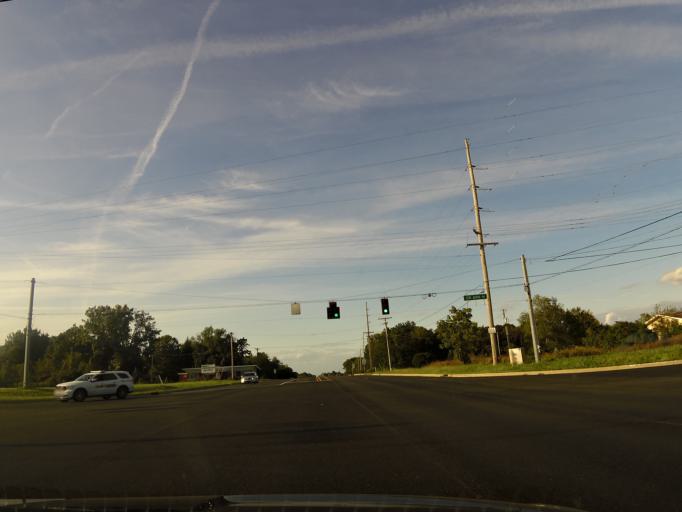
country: US
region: Indiana
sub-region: Tippecanoe County
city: Battle Ground
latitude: 40.5039
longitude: -86.8685
